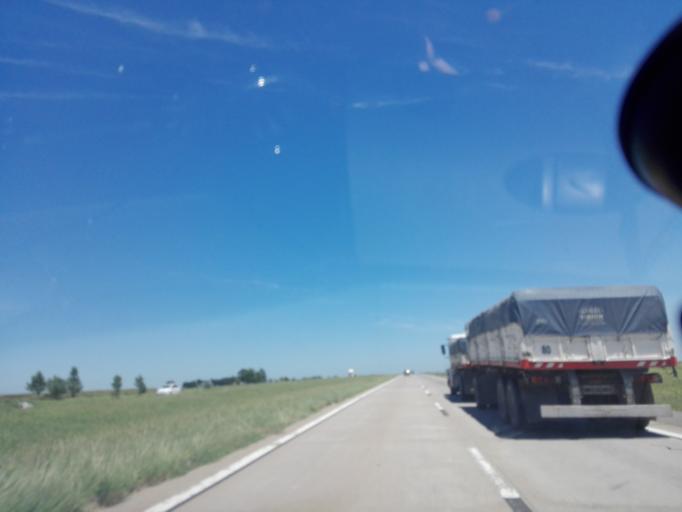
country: AR
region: Santa Fe
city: Armstrong
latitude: -32.8234
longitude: -61.5251
